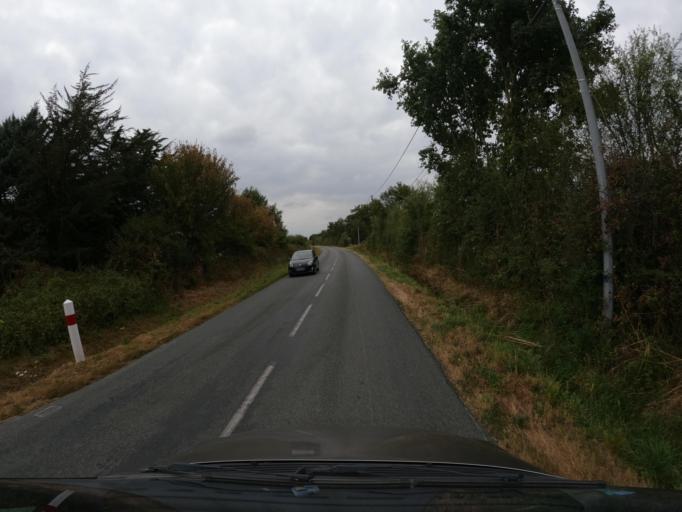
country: FR
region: Pays de la Loire
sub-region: Departement de la Vendee
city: Tiffauges
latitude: 47.0015
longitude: -1.0954
